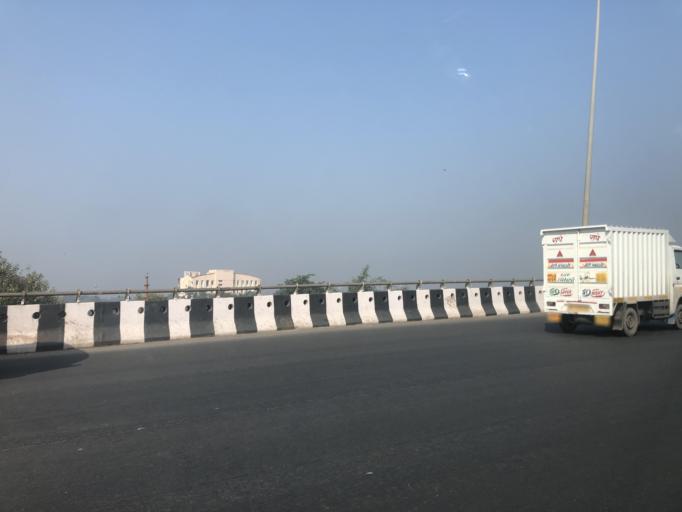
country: IN
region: Haryana
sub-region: Gurgaon
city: Gurgaon
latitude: 28.5424
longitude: 77.1179
